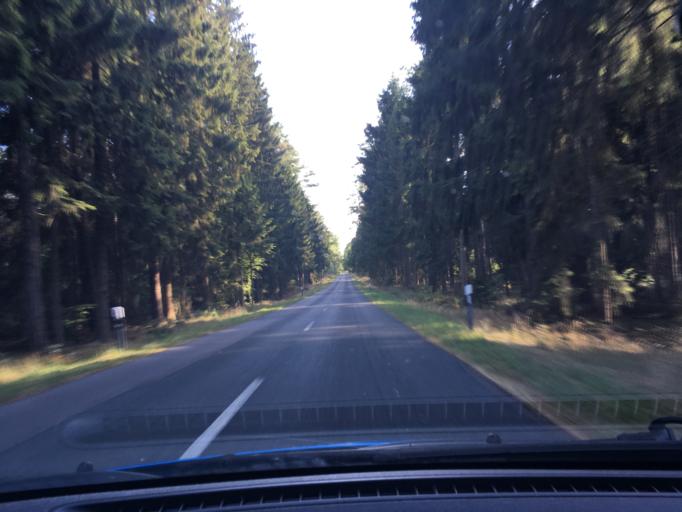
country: DE
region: Lower Saxony
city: Thomasburg
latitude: 53.2449
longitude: 10.7069
